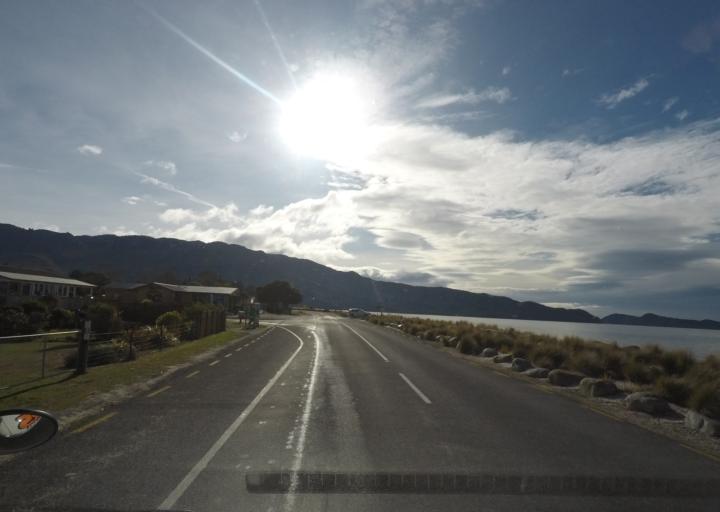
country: NZ
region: Tasman
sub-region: Tasman District
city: Motueka
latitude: -41.0059
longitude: 173.0097
